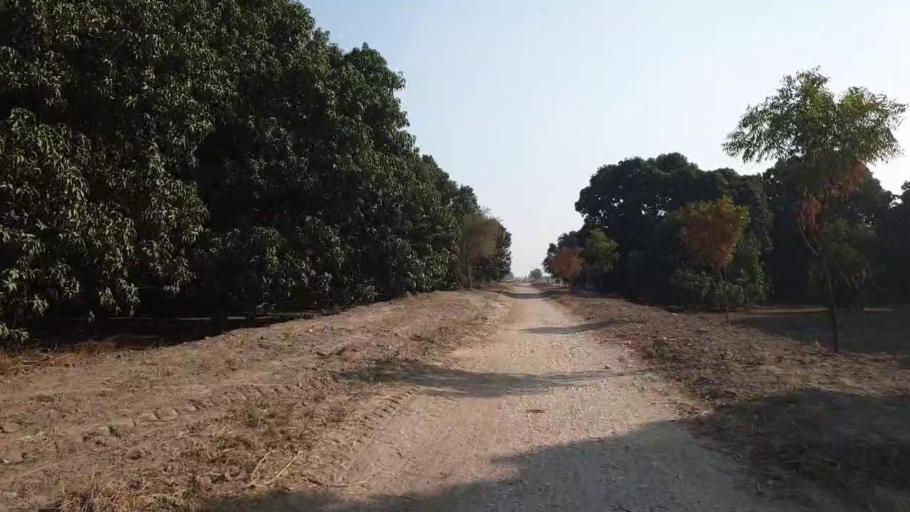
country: PK
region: Sindh
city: Tando Adam
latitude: 25.6016
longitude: 68.6161
